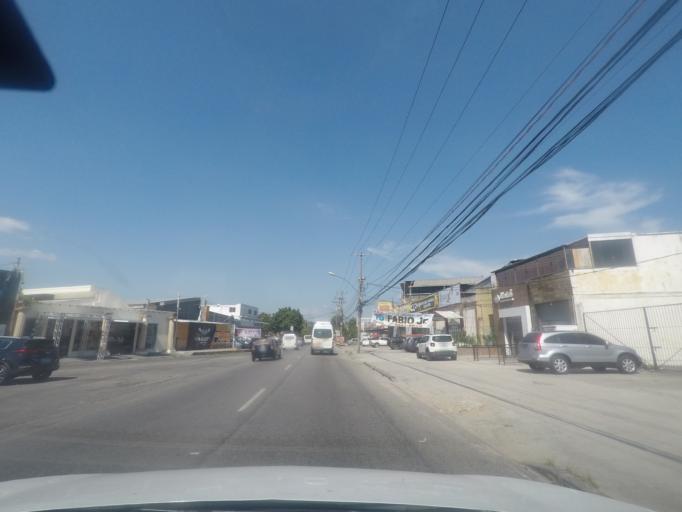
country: BR
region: Rio de Janeiro
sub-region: Nilopolis
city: Nilopolis
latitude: -22.8787
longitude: -43.4497
